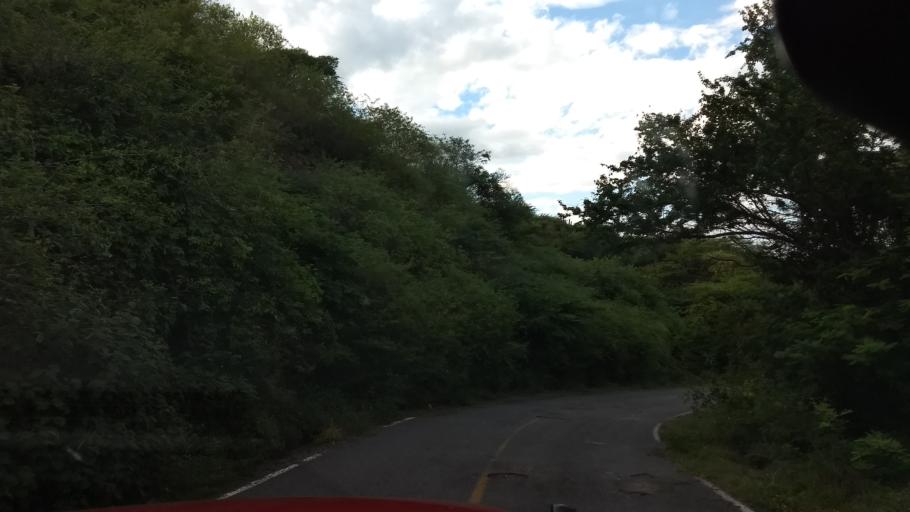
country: MX
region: Colima
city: Suchitlan
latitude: 19.4516
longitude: -103.8207
